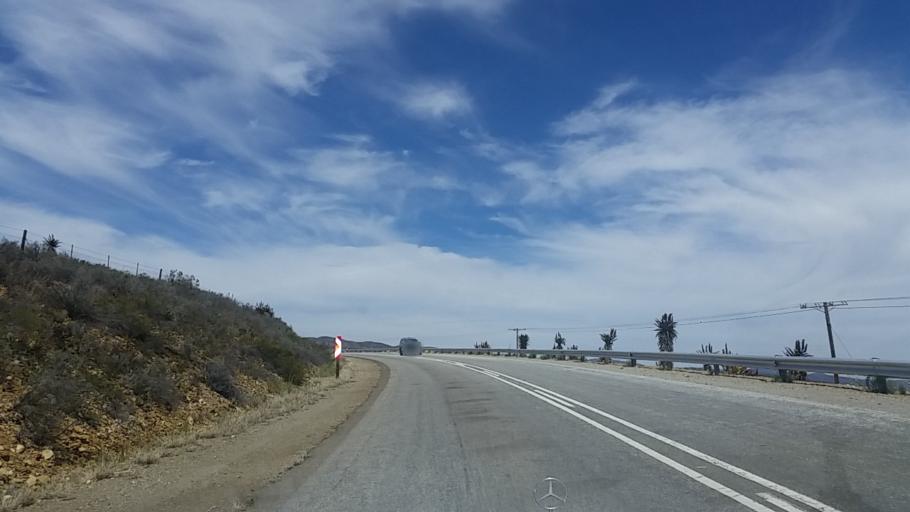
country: ZA
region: Western Cape
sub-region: Eden District Municipality
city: Knysna
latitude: -33.6307
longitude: 23.1276
